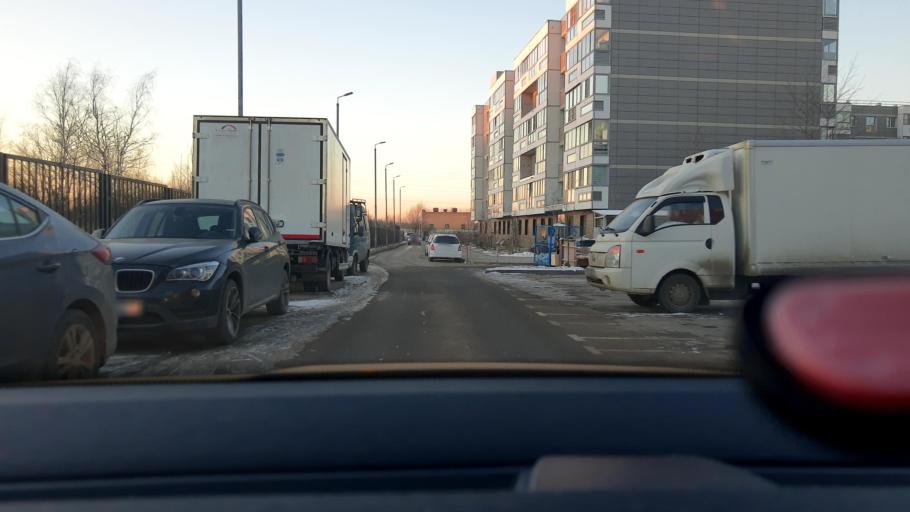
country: RU
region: Moskovskaya
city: Nemchinovka
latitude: 55.7235
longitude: 37.3254
